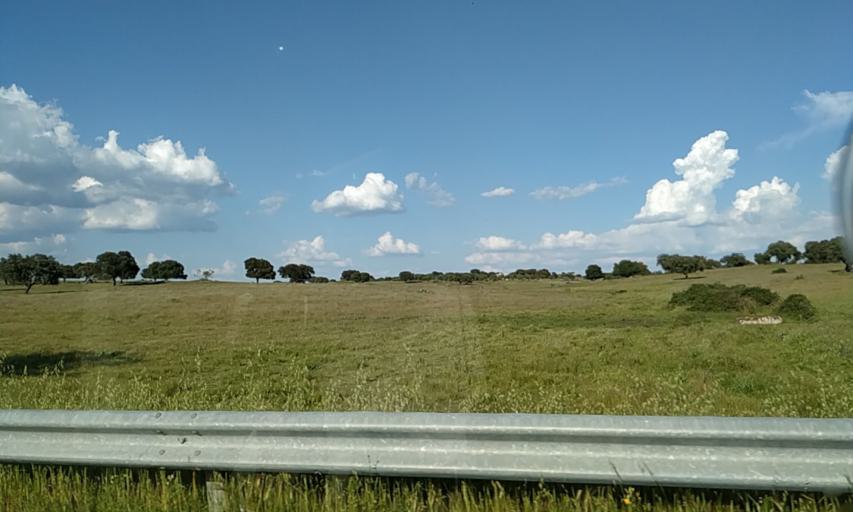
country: PT
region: Portalegre
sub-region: Portalegre
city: Urra
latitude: 39.1082
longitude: -7.4392
